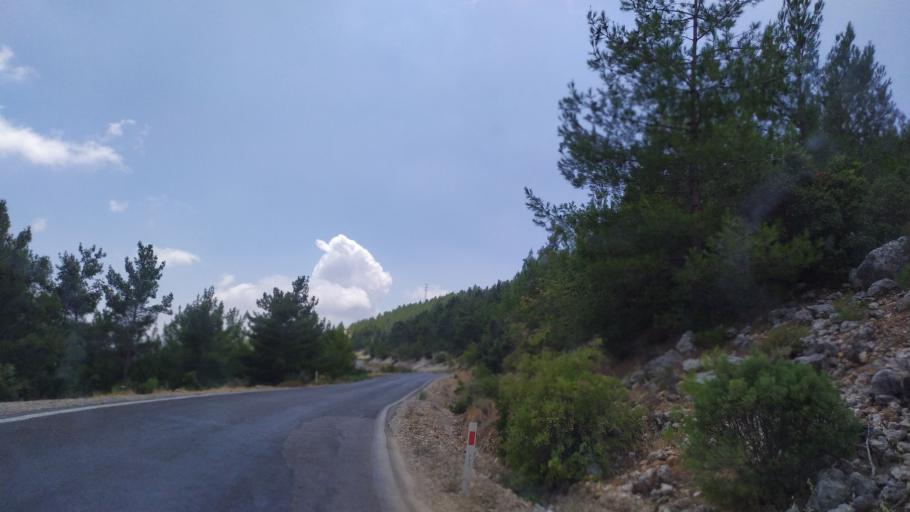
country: TR
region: Mersin
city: Gulnar
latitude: 36.2949
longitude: 33.3801
